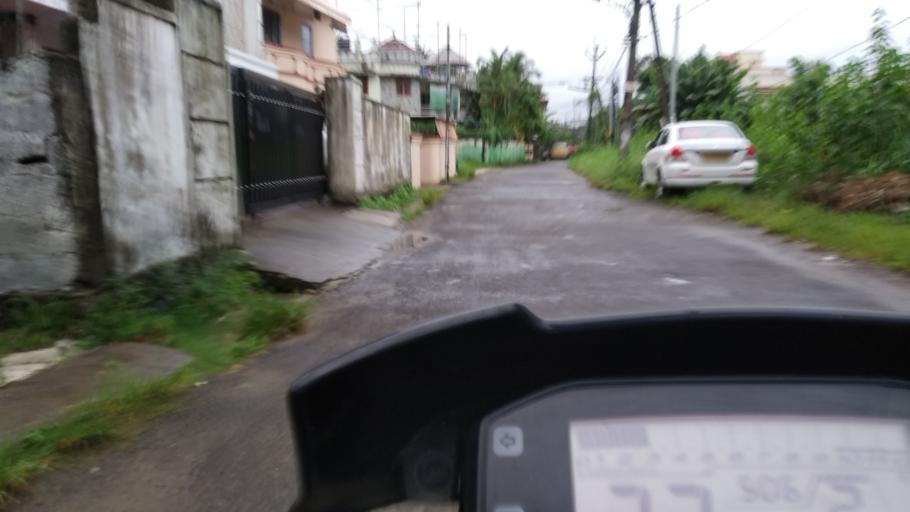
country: IN
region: Kerala
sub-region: Ernakulam
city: Cochin
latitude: 9.9775
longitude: 76.3071
